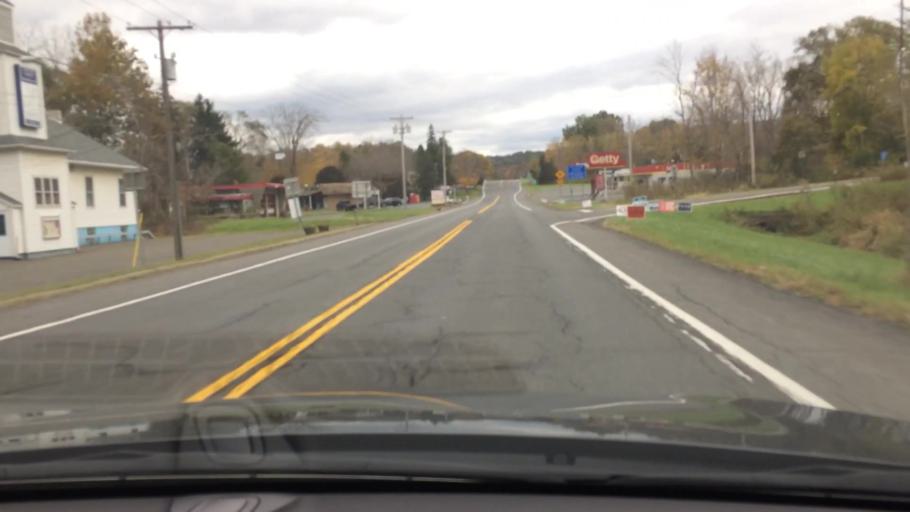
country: US
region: New York
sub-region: Columbia County
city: Philmont
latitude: 42.1209
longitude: -73.7188
